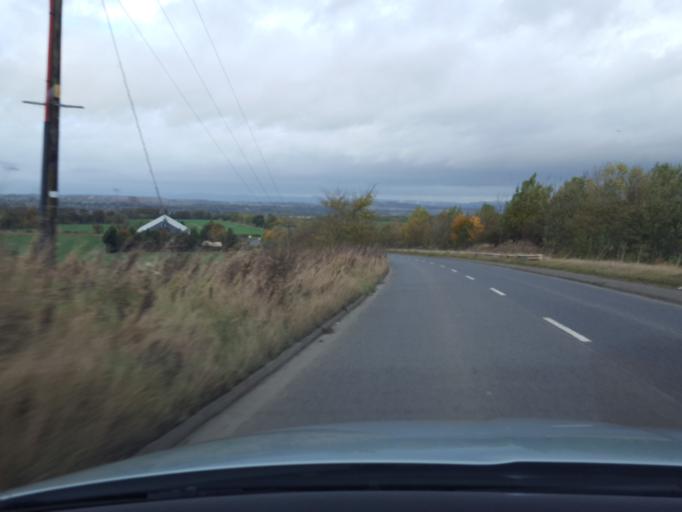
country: GB
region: Scotland
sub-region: Edinburgh
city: Newbridge
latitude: 55.9117
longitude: -3.4067
